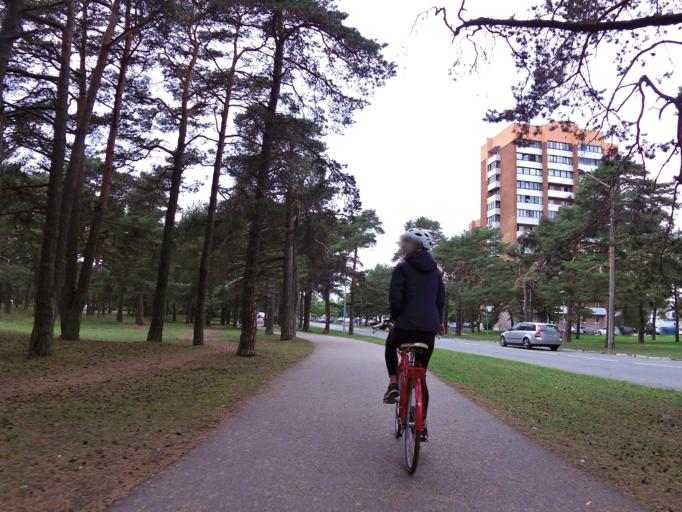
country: EE
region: Harju
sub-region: Tallinna linn
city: Tallinn
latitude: 59.4414
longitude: 24.6901
